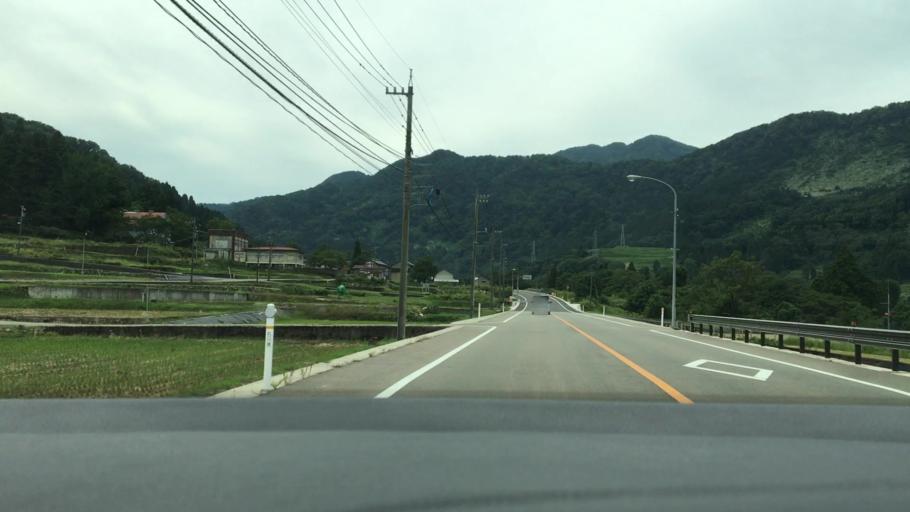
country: JP
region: Ishikawa
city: Tsurugi-asahimachi
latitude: 36.3108
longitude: 136.6454
